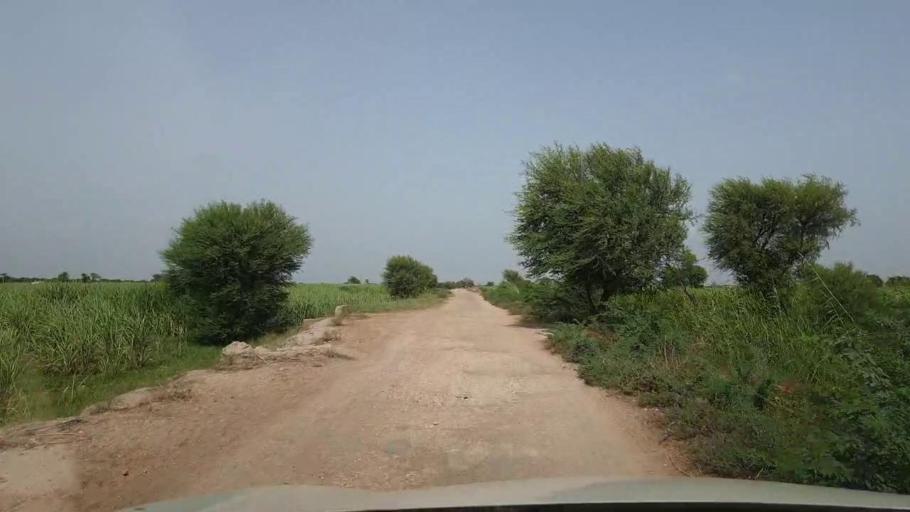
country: PK
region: Sindh
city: Mirwah Gorchani
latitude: 25.2559
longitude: 68.9659
